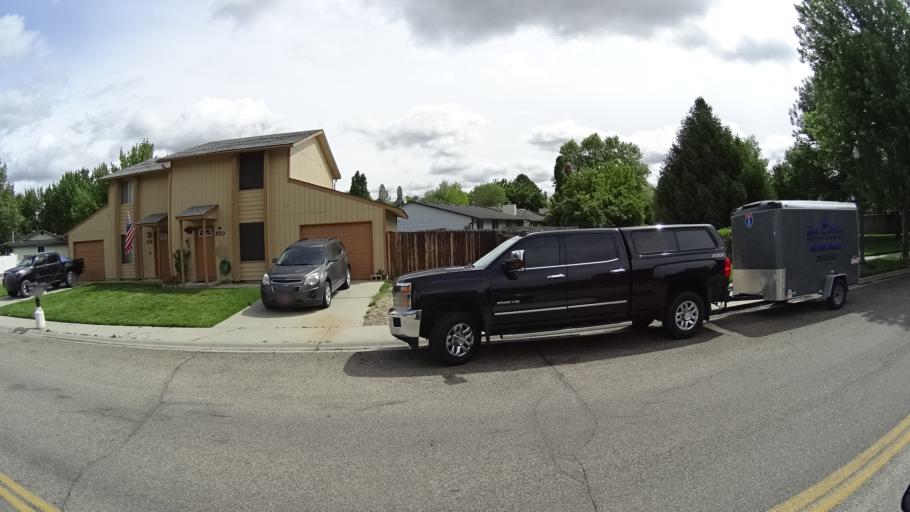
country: US
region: Idaho
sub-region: Ada County
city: Eagle
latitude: 43.6967
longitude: -116.3477
